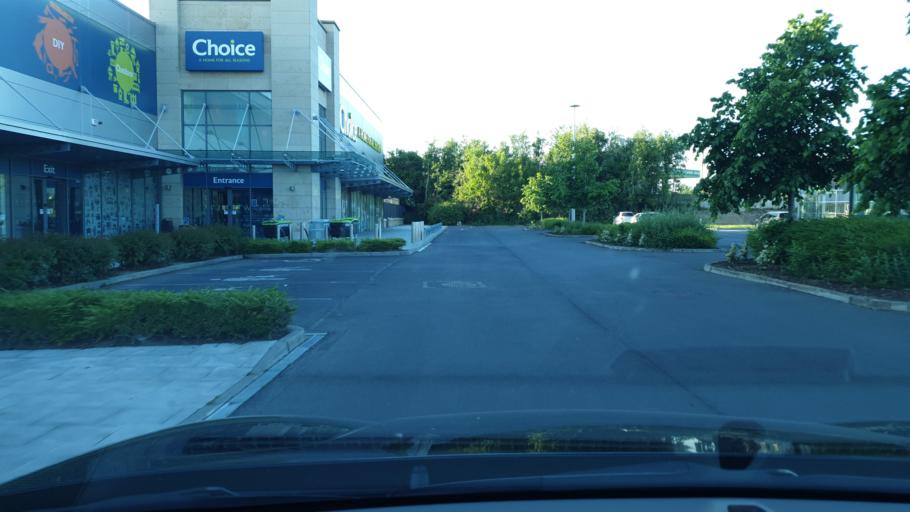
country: IE
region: Leinster
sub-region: An Mhi
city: Ashbourne
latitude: 53.5229
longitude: -6.4151
